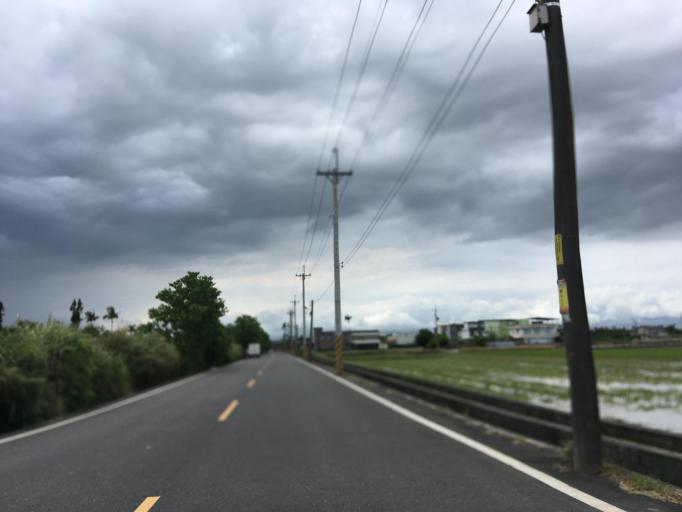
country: TW
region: Taiwan
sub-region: Yilan
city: Yilan
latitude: 24.6874
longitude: 121.8074
